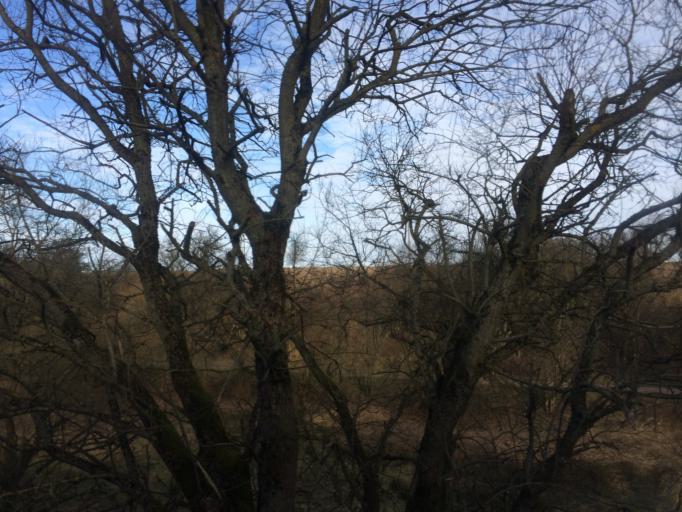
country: DK
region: South Denmark
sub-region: Vejle Kommune
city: Jelling
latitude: 55.7679
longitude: 9.4546
